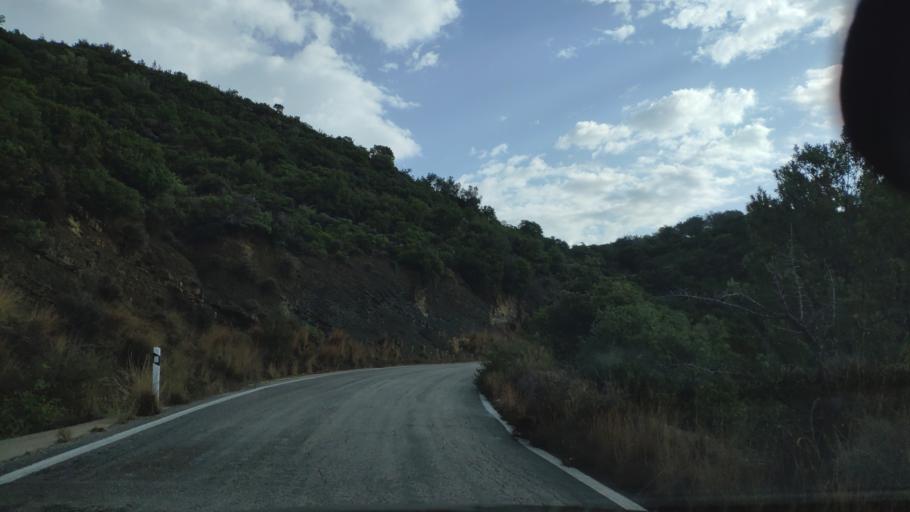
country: GR
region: West Greece
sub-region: Nomos Aitolias kai Akarnanias
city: Sardinia
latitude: 38.8889
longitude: 21.2388
